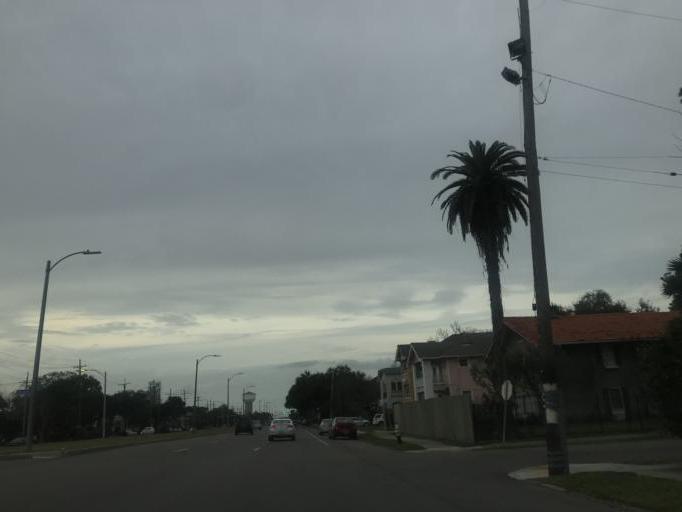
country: US
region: Louisiana
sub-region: Jefferson Parish
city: Jefferson
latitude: 29.9539
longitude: -90.1178
